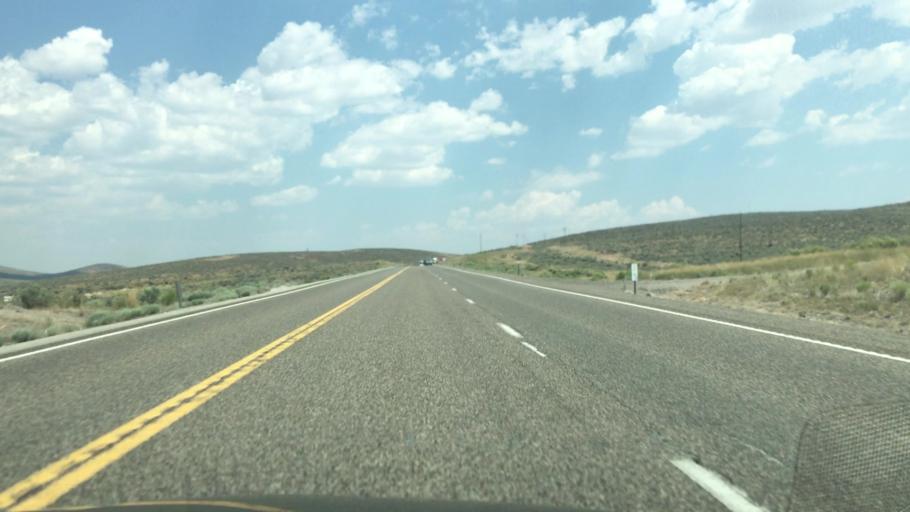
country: US
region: Nevada
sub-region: Elko County
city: Wells
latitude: 41.1803
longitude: -114.8767
